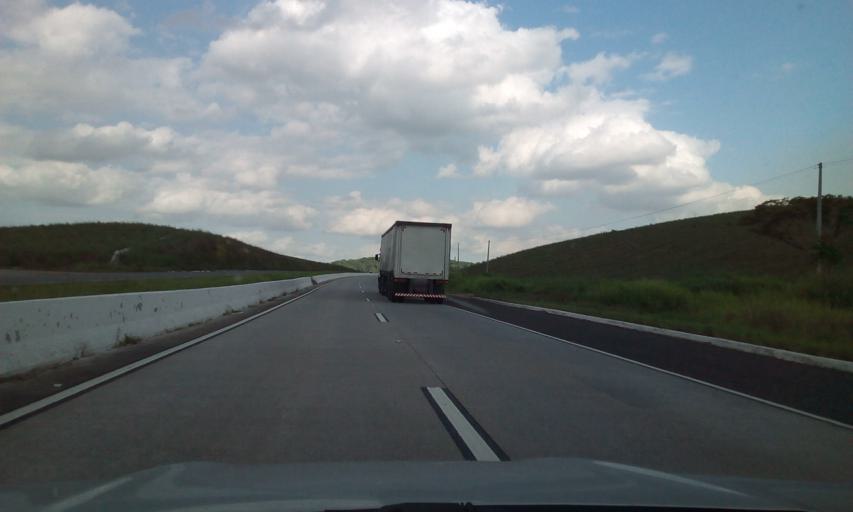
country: BR
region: Pernambuco
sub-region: Joaquim Nabuco
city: Joaquim Nabuco
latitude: -8.5898
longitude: -35.5121
